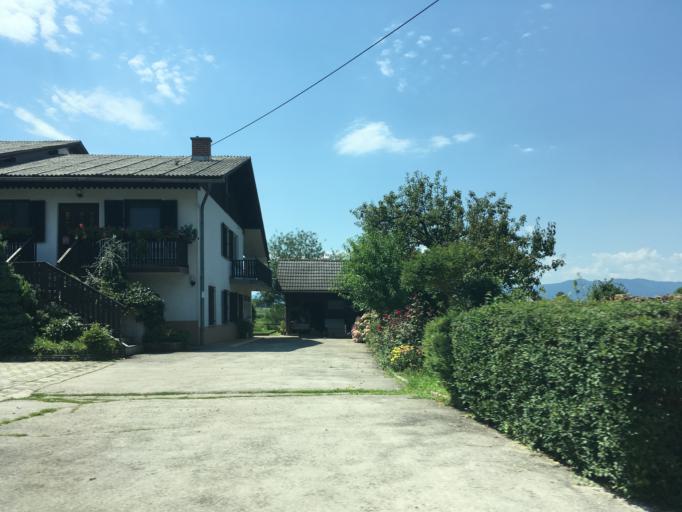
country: SI
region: Metlika
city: Metlika
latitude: 45.6196
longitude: 15.3222
